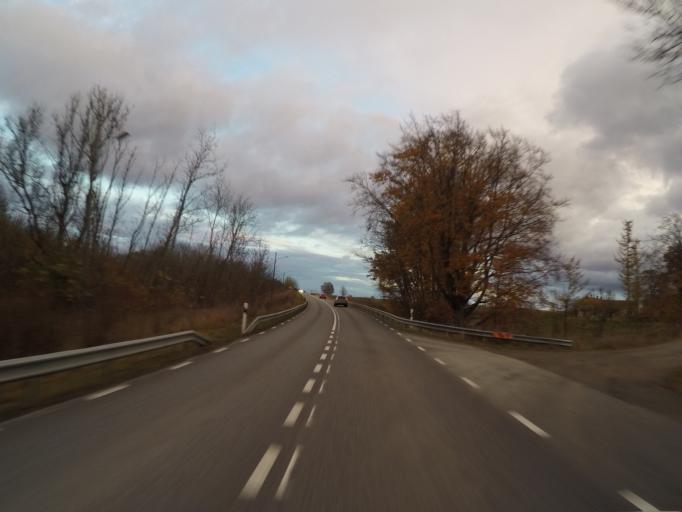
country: SE
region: Skane
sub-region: Kristianstads Kommun
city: Degeberga
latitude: 55.8971
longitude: 14.0740
